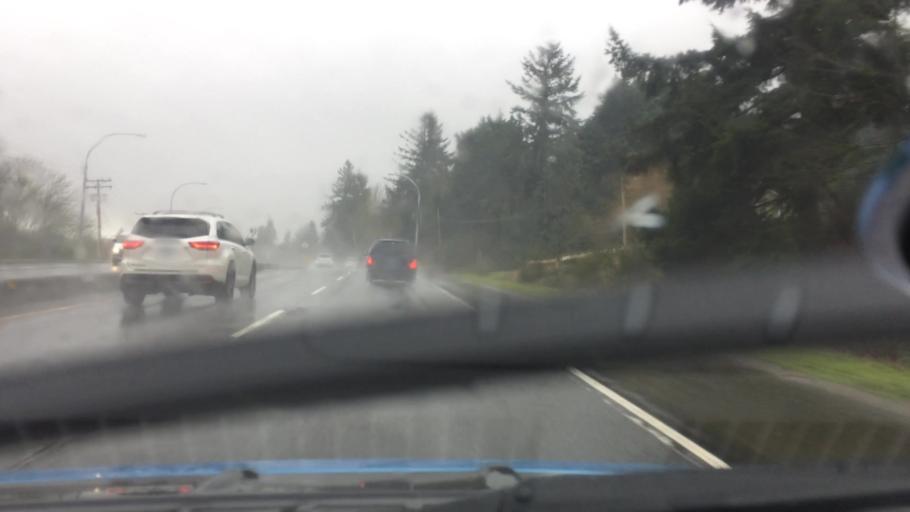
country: CA
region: British Columbia
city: North Saanich
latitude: 48.5668
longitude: -123.3988
